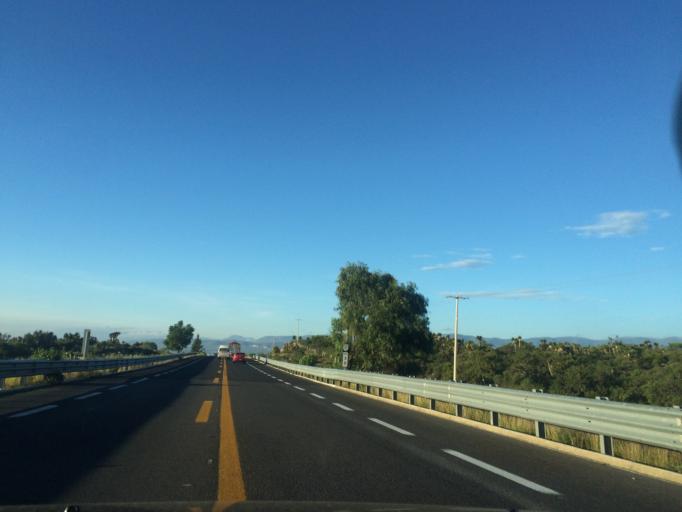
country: MX
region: Puebla
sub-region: Tehuacan
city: Magdalena Cuayucatepec
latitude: 18.5733
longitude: -97.4643
